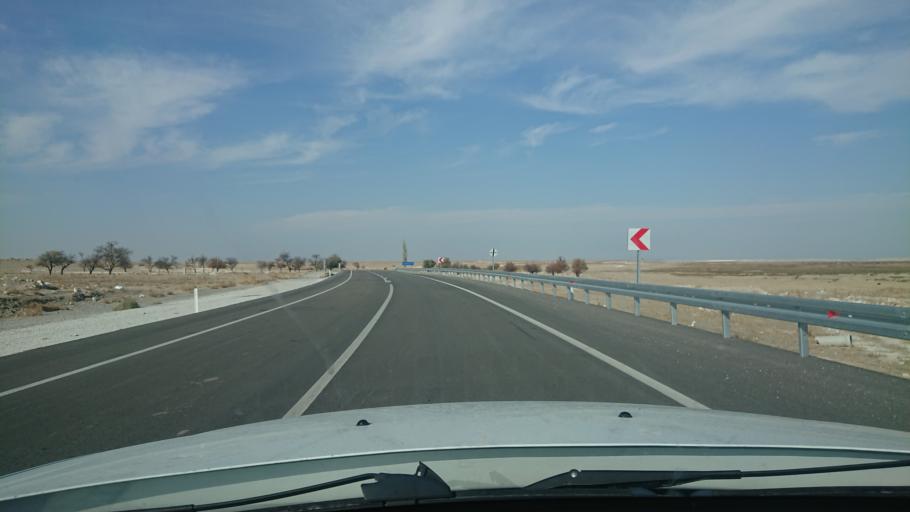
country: TR
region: Aksaray
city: Sultanhani
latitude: 38.2714
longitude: 33.4373
